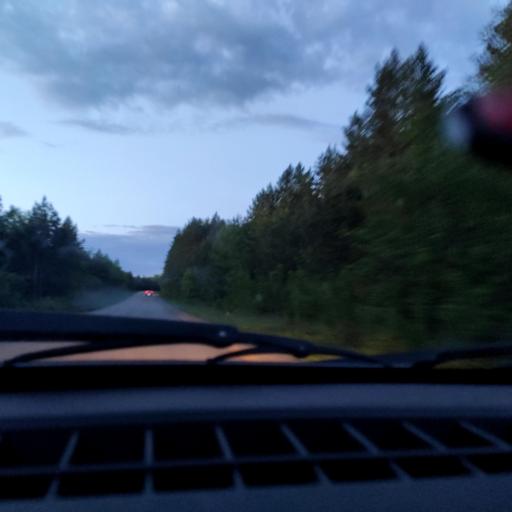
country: RU
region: Bashkortostan
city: Avdon
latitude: 54.6453
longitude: 55.5725
